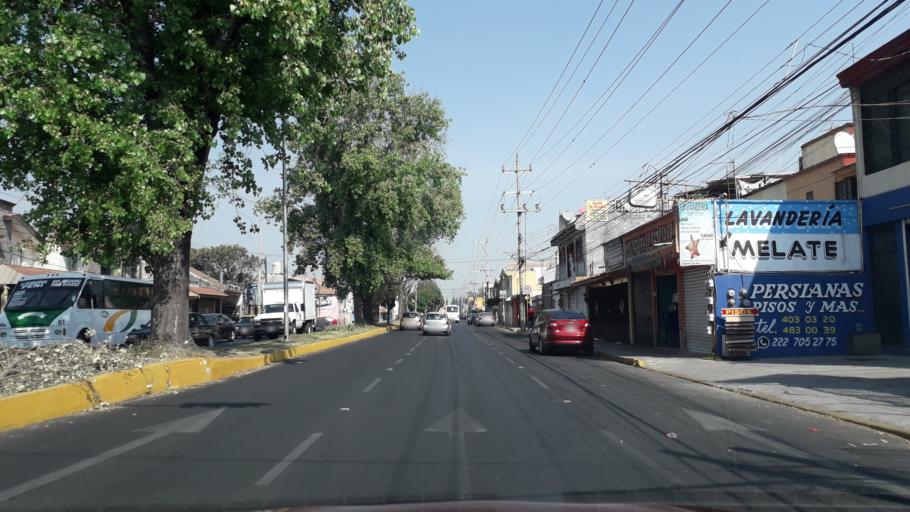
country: MX
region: Puebla
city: Puebla
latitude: 19.0678
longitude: -98.2176
